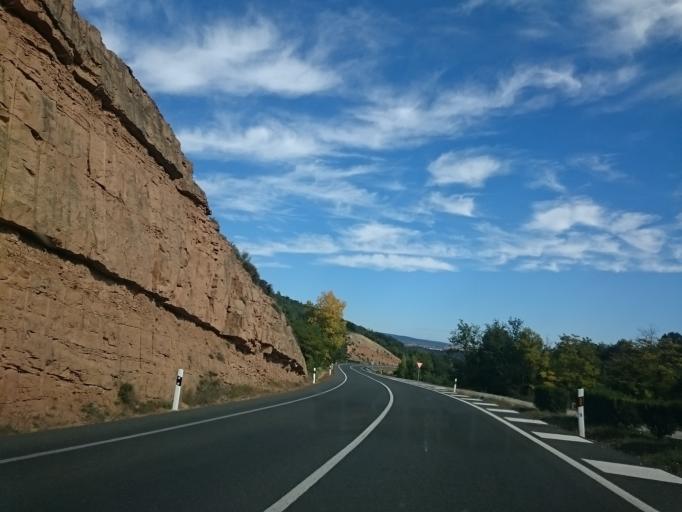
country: ES
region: Aragon
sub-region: Provincia de Huesca
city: Benavarri / Benabarre
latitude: 42.0682
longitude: 0.4749
